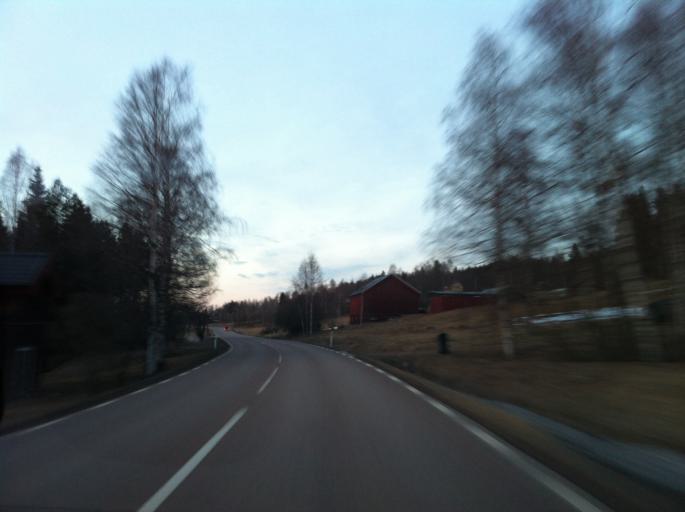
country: SE
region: Dalarna
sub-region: Orsa Kommun
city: Orsa
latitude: 61.0714
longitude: 14.6190
